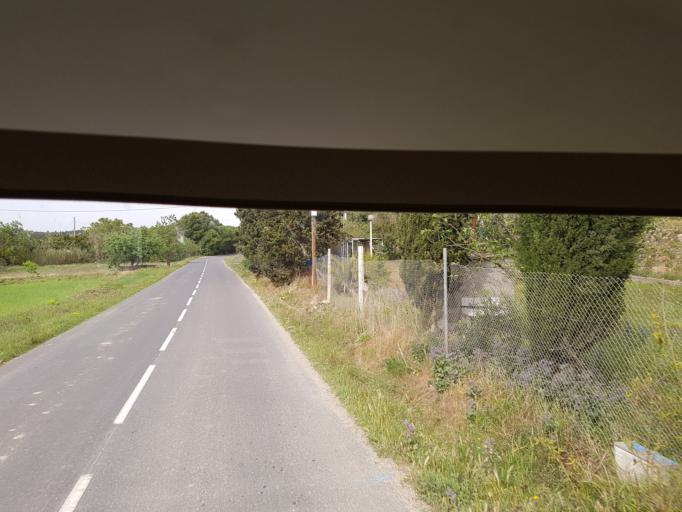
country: FR
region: Languedoc-Roussillon
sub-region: Departement de l'Herault
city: Lespignan
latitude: 43.2658
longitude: 3.1648
